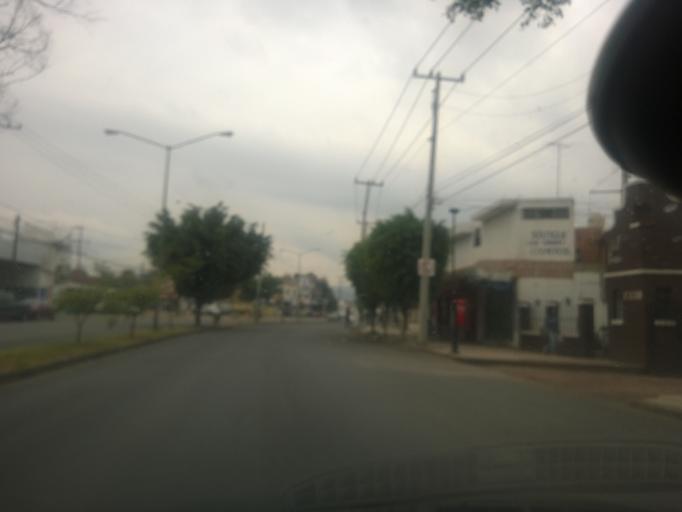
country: MX
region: Guanajuato
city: Leon
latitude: 21.1504
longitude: -101.6553
